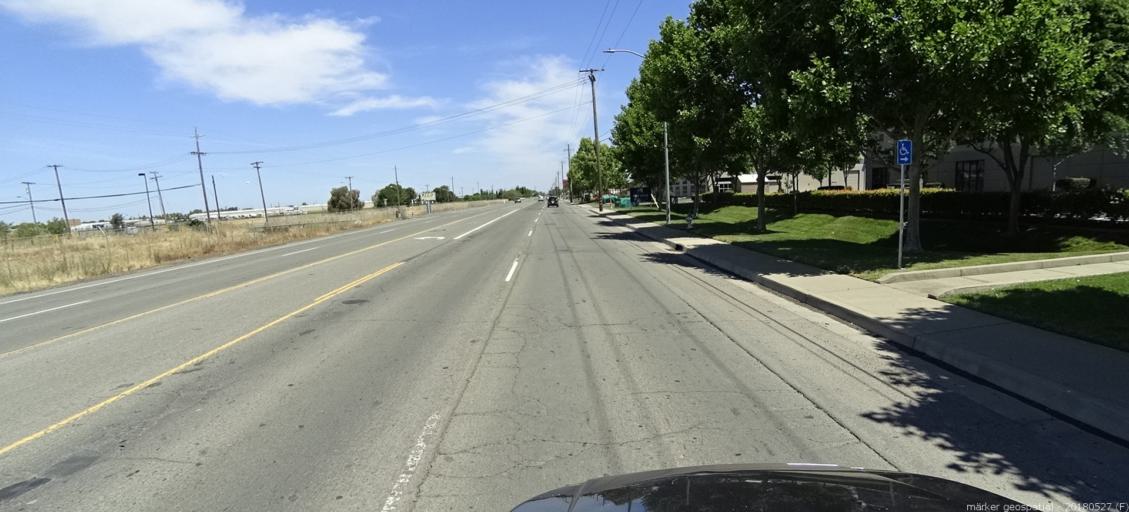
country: US
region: California
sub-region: Sacramento County
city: Florin
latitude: 38.5121
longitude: -121.3905
